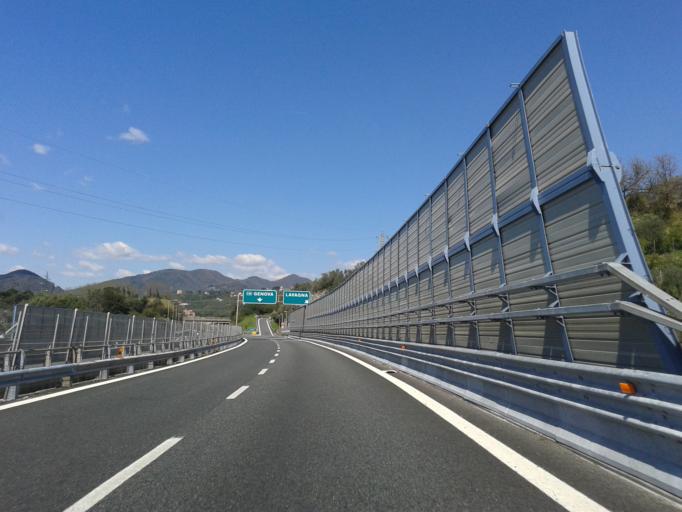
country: IT
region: Liguria
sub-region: Provincia di Genova
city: Lavagna
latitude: 44.3157
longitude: 9.3541
